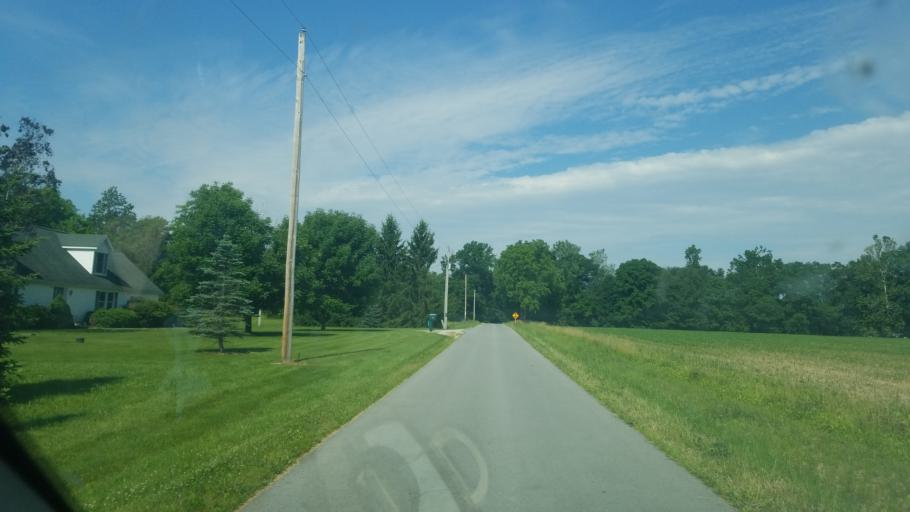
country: US
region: Ohio
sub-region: Wyandot County
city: Carey
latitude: 40.9563
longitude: -83.2969
